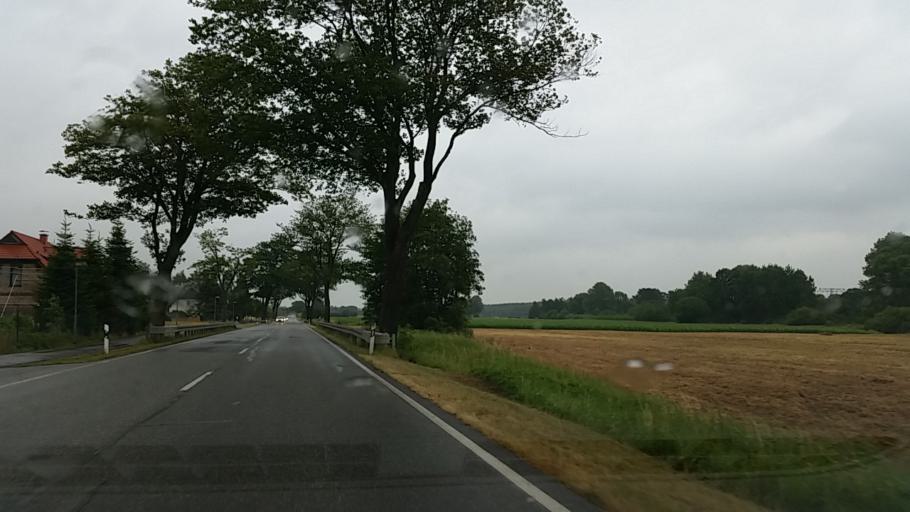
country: DE
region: Mecklenburg-Vorpommern
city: Biendorf
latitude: 54.0512
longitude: 11.7307
